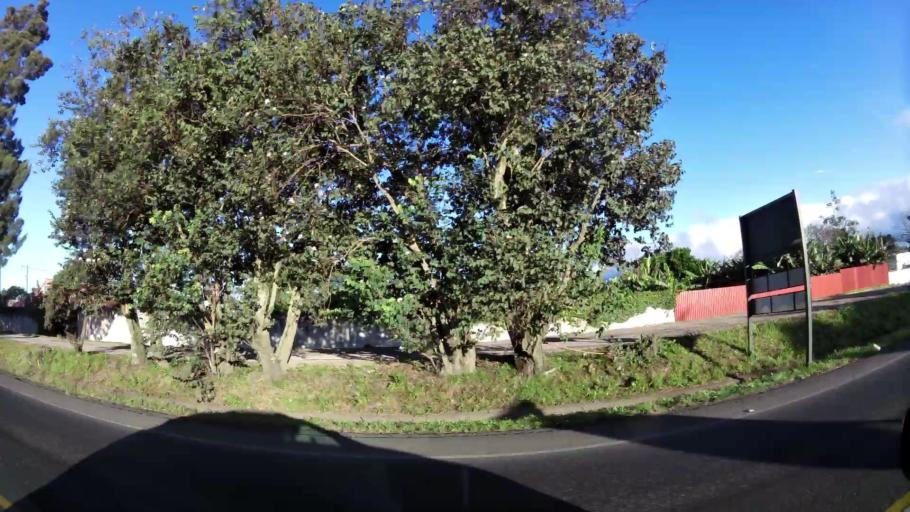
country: CR
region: Heredia
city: Angeles
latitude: 9.9918
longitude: -84.0393
